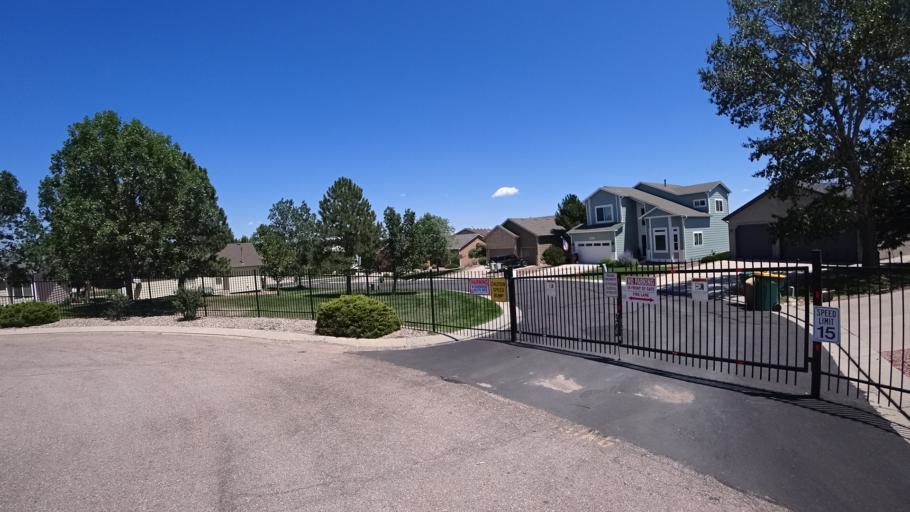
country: US
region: Colorado
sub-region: El Paso County
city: Air Force Academy
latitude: 38.9194
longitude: -104.8343
